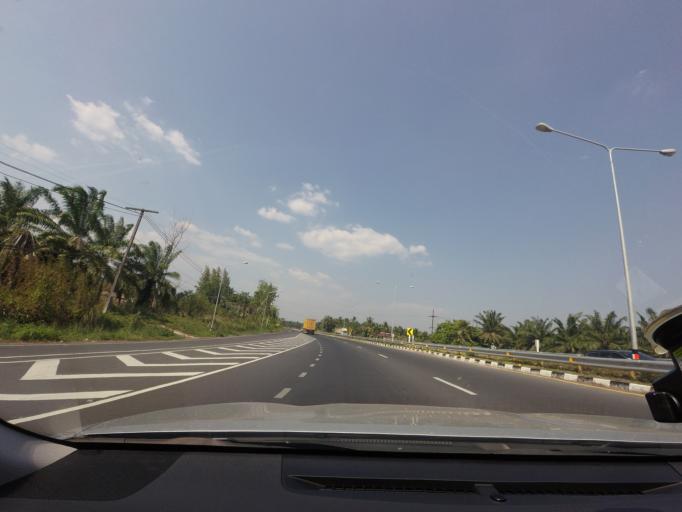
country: TH
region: Phangnga
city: Thap Put
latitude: 8.5153
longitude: 98.6999
